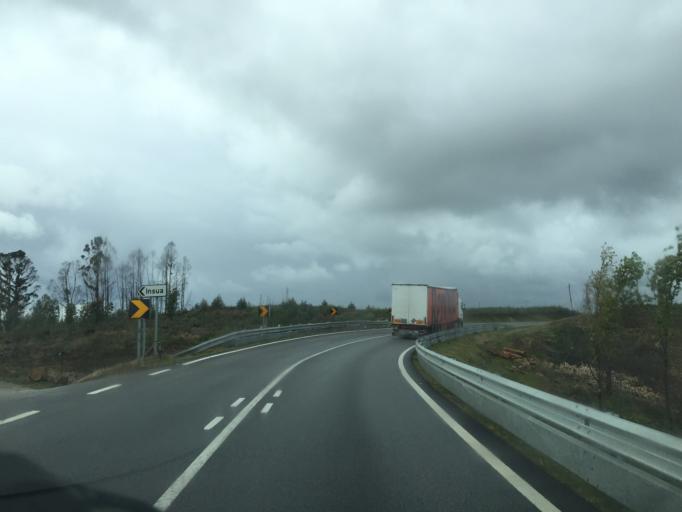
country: PT
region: Coimbra
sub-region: Oliveira do Hospital
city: Oliveira do Hospital
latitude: 40.3172
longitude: -7.9117
